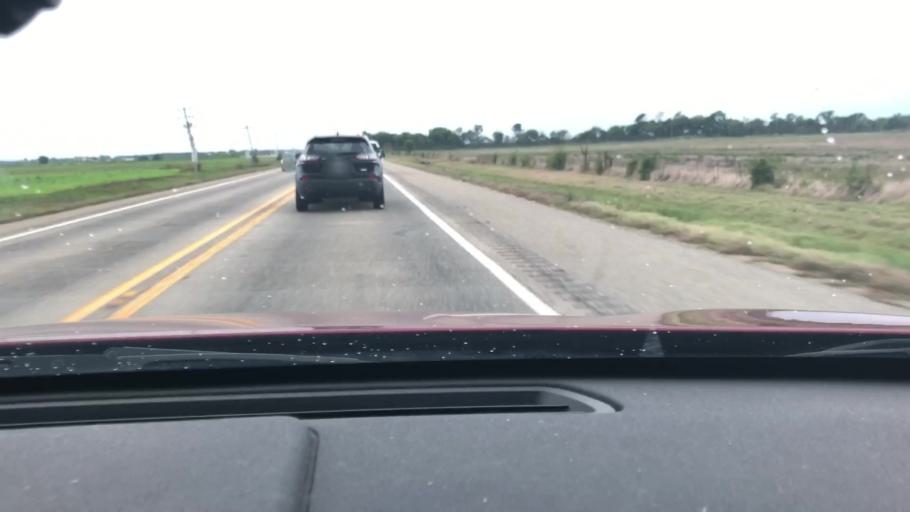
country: US
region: Arkansas
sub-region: Lafayette County
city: Lewisville
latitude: 33.4021
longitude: -93.7444
